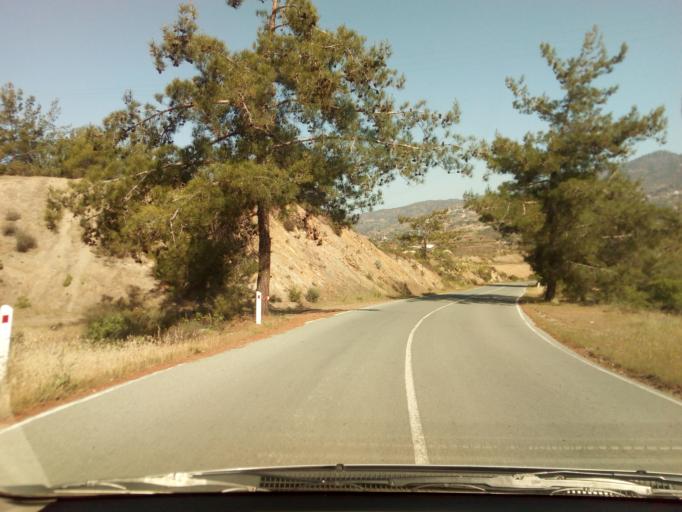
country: CY
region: Limassol
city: Pelendri
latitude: 34.8406
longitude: 33.0313
